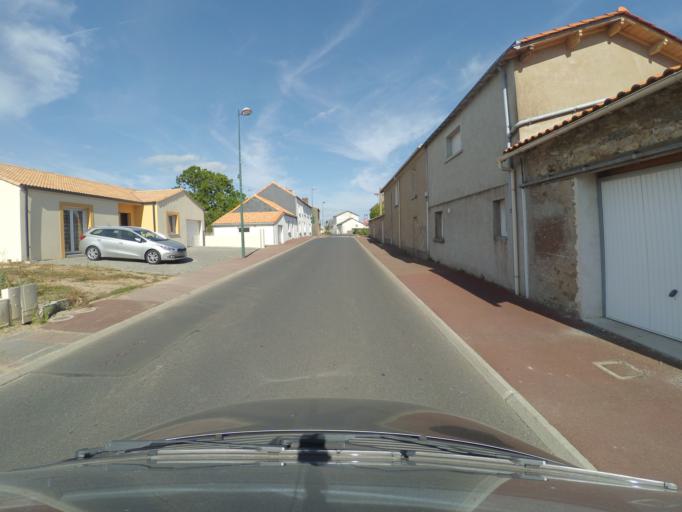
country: FR
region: Pays de la Loire
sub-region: Departement de la Loire-Atlantique
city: Le Bignon
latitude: 47.0970
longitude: -1.4938
